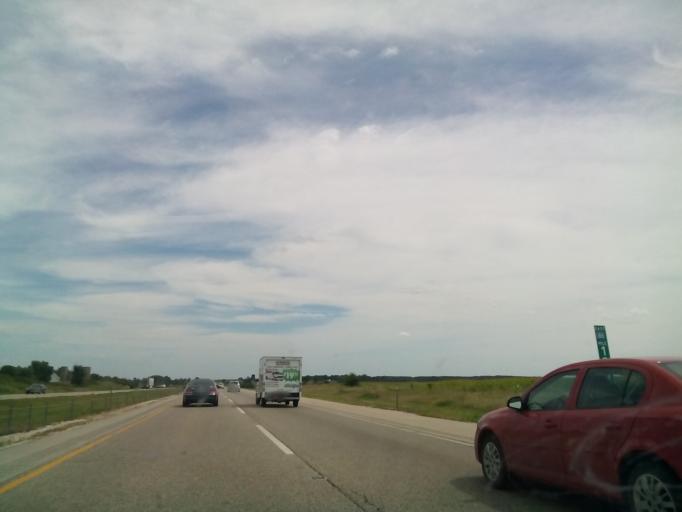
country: US
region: Illinois
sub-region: Kane County
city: Maple Park
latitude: 41.8714
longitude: -88.5936
